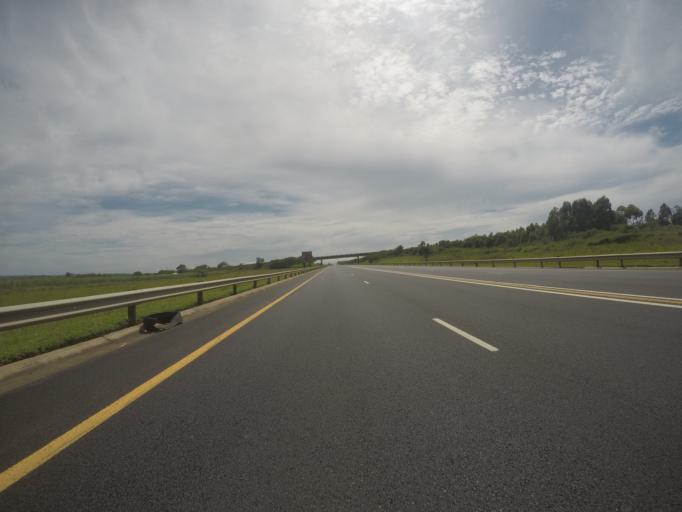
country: ZA
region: KwaZulu-Natal
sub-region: iLembe District Municipality
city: Mandeni
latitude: -29.1553
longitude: 31.5393
